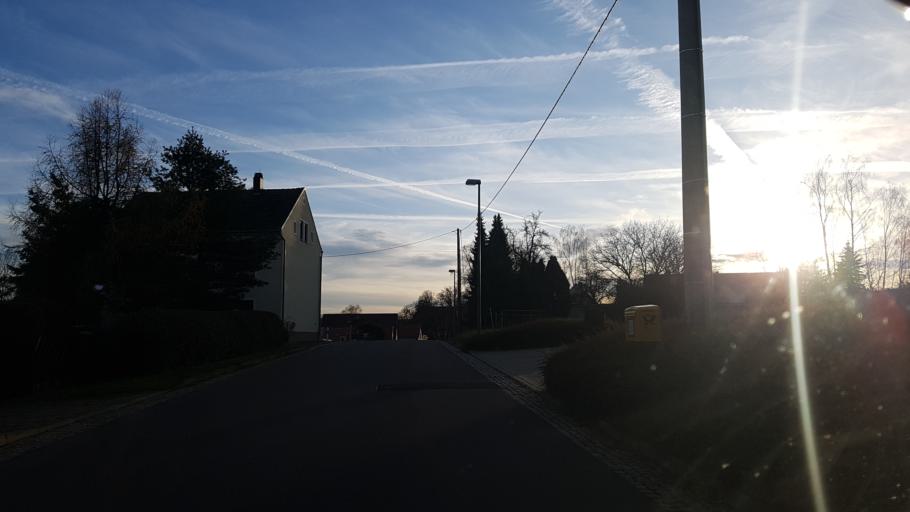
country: DE
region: Saxony
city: Ostrau
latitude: 51.1692
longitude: 13.1622
